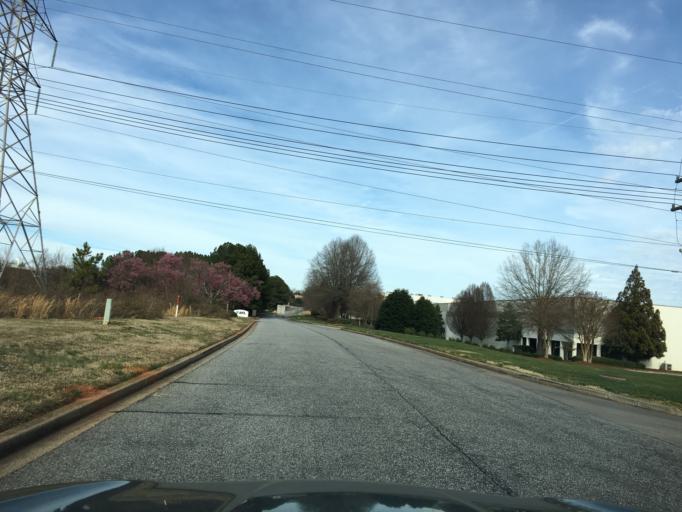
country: US
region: South Carolina
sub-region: Spartanburg County
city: Wellford
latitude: 34.8993
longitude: -82.1072
